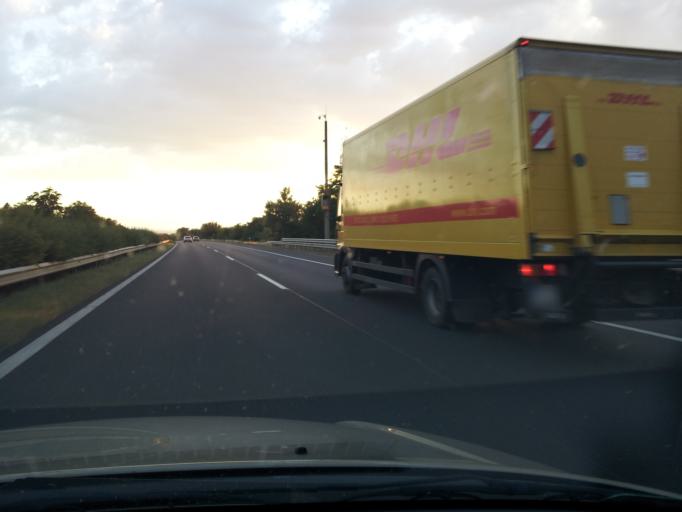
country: HU
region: Pest
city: Fot
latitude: 47.5936
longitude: 19.2090
